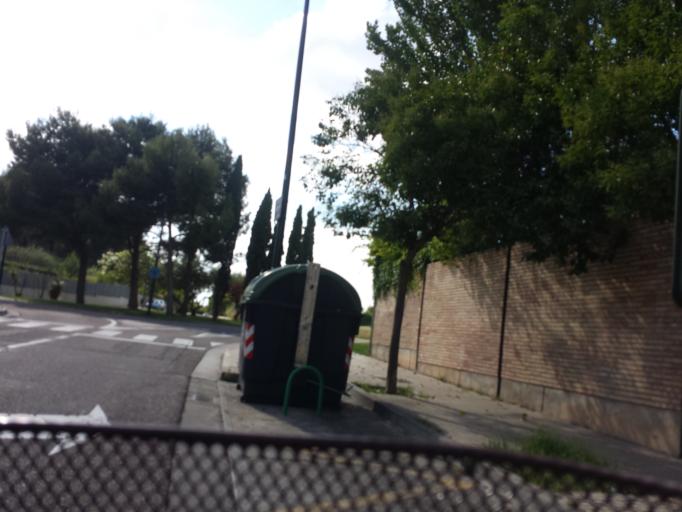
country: ES
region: Aragon
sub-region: Provincia de Zaragoza
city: Delicias
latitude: 41.6300
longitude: -0.9167
